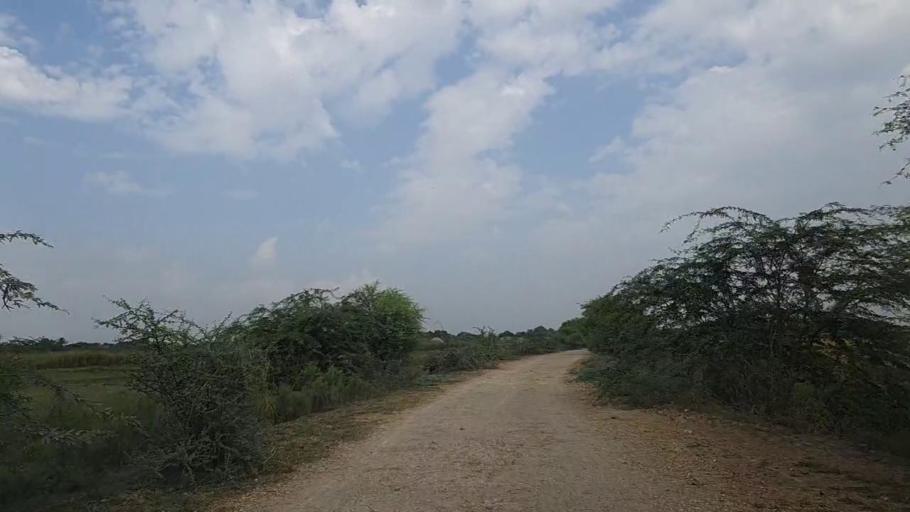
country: PK
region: Sindh
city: Daro Mehar
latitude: 24.7138
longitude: 68.1540
